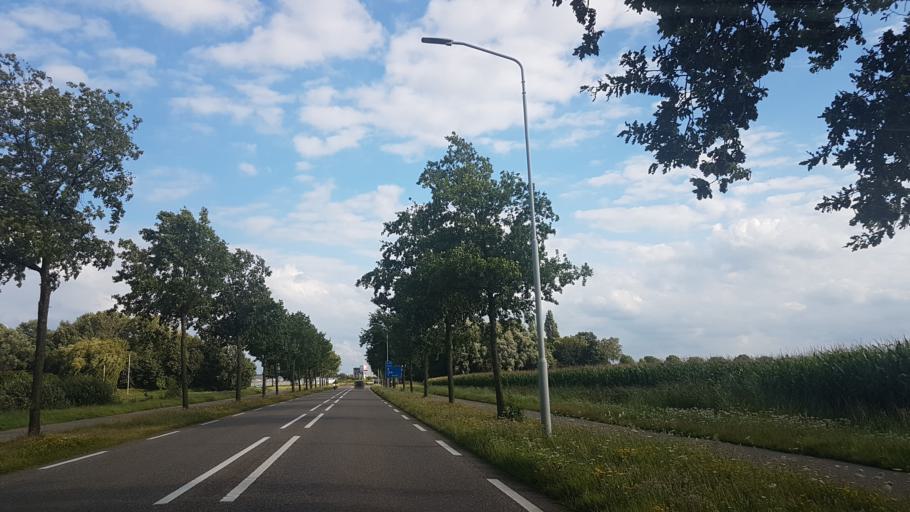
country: NL
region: North Brabant
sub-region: Gemeente Made en Drimmelen
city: Made
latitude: 51.6834
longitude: 4.8159
